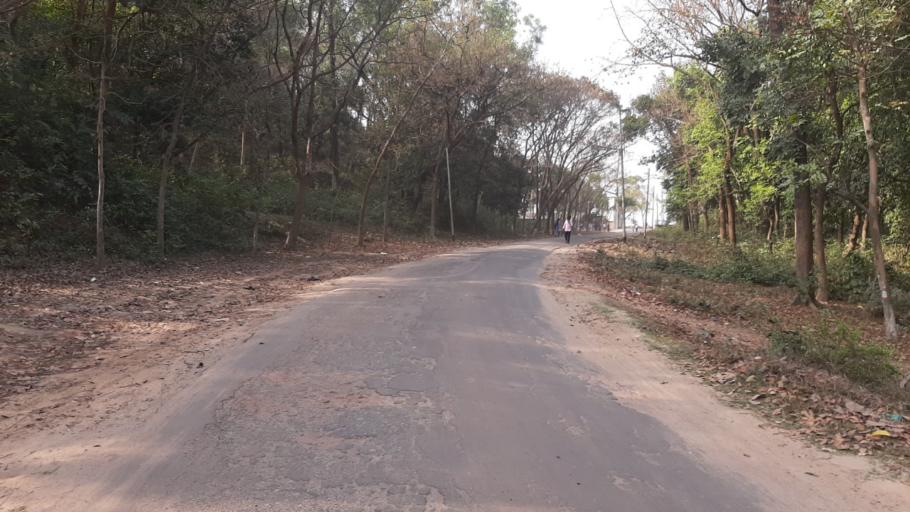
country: BD
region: Chittagong
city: Raojan
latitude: 22.4769
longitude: 91.7911
